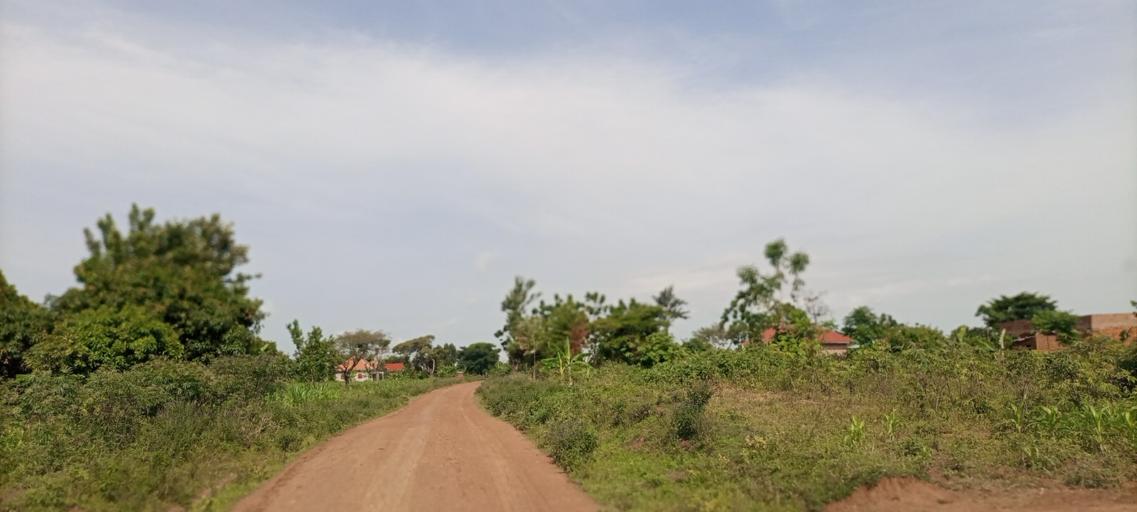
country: UG
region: Eastern Region
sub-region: Mbale District
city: Mbale
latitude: 1.1331
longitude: 34.0521
